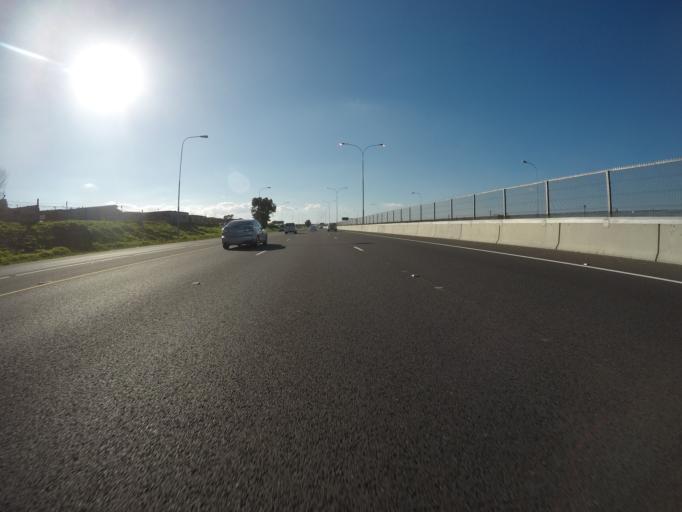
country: ZA
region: Western Cape
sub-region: City of Cape Town
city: Kraaifontein
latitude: -33.9753
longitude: 18.6530
